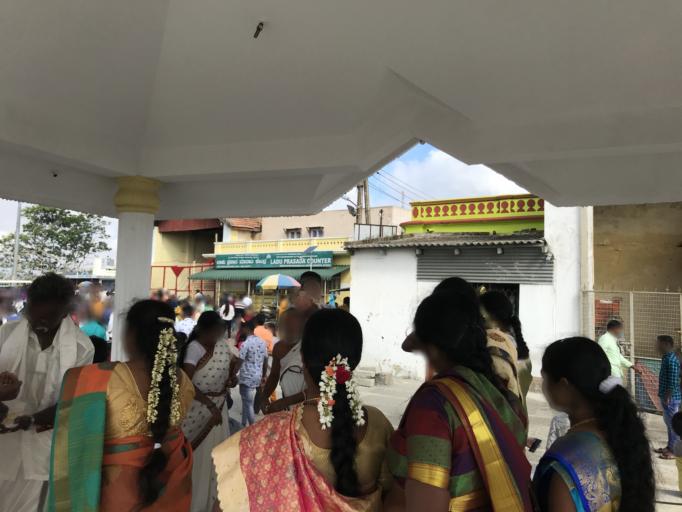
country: IN
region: Karnataka
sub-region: Mysore
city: Mysore
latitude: 12.2725
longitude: 76.6712
